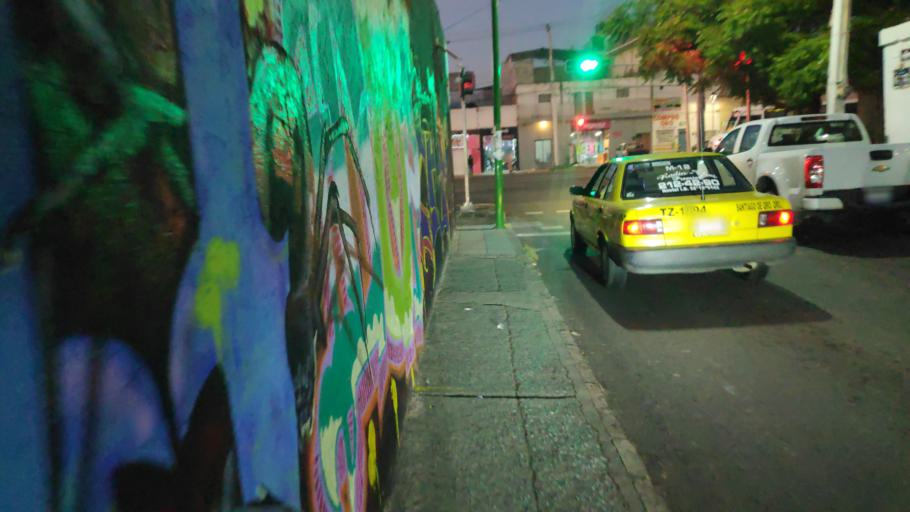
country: MX
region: Queretaro
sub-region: Queretaro
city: Santiago de Queretaro
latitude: 20.5911
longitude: -100.3812
